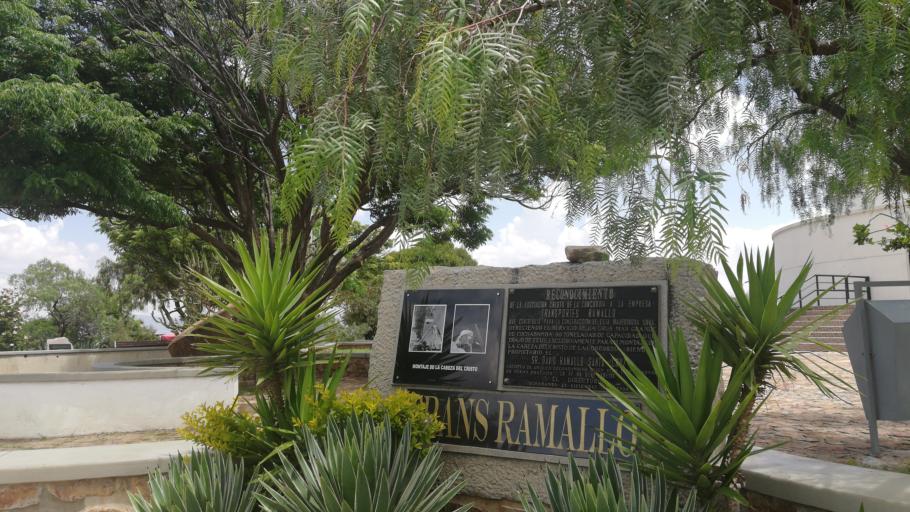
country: BO
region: Cochabamba
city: Cochabamba
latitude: -17.3844
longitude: -66.1345
